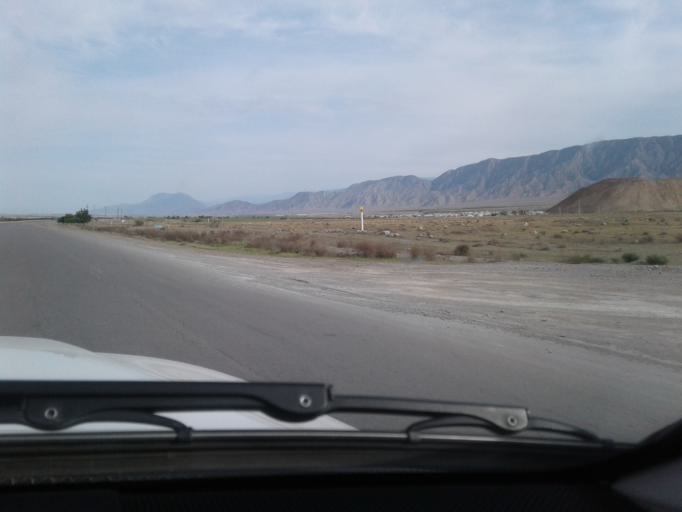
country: TM
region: Ahal
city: Arcabil
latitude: 38.2172
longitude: 57.8052
